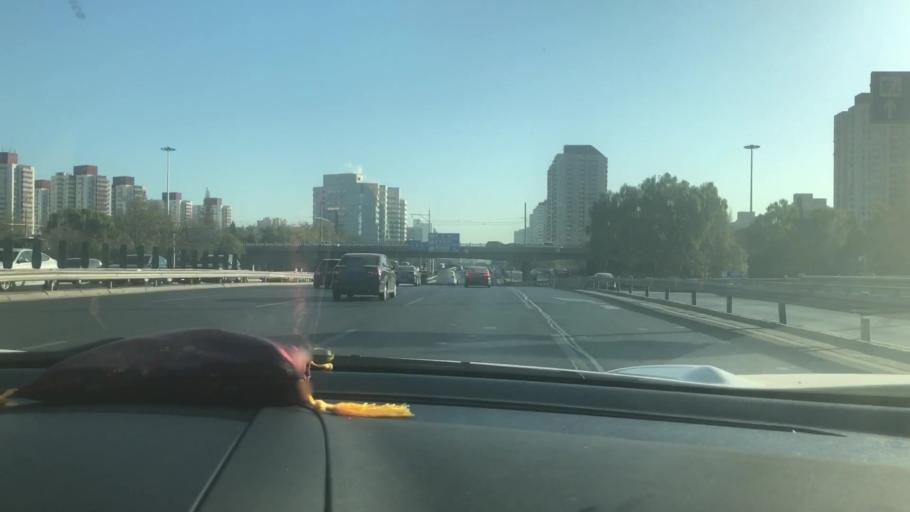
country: CN
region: Beijing
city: Datun
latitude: 39.9868
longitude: 116.3996
